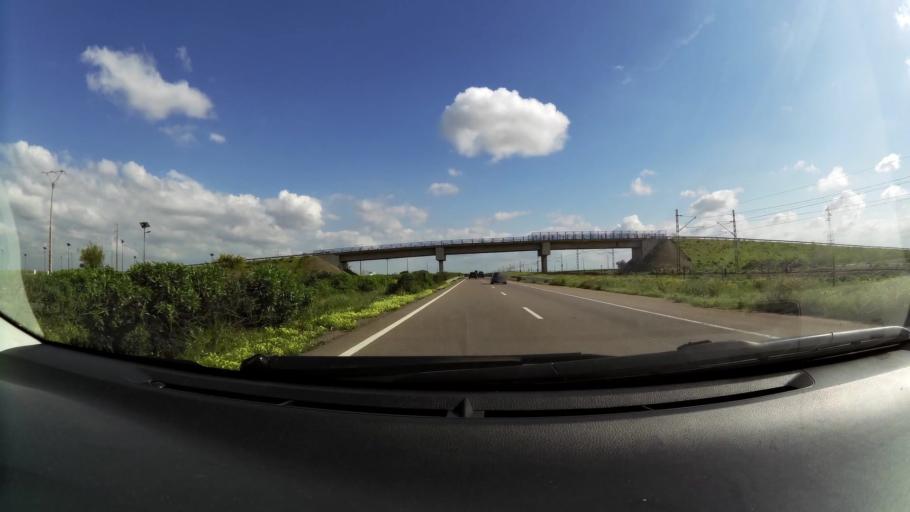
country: MA
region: Chaouia-Ouardigha
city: Nouaseur
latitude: 33.3565
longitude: -7.6177
